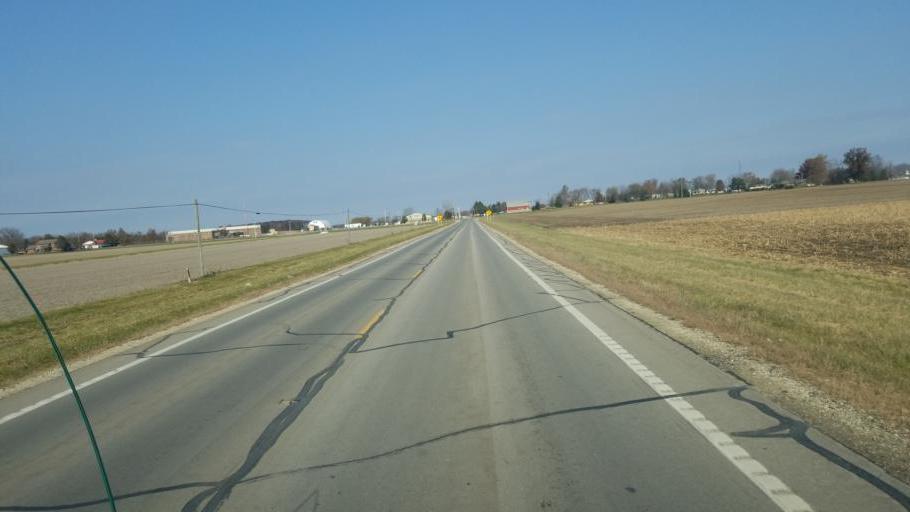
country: US
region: Ohio
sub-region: Mercer County
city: Celina
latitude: 40.5409
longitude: -84.6285
